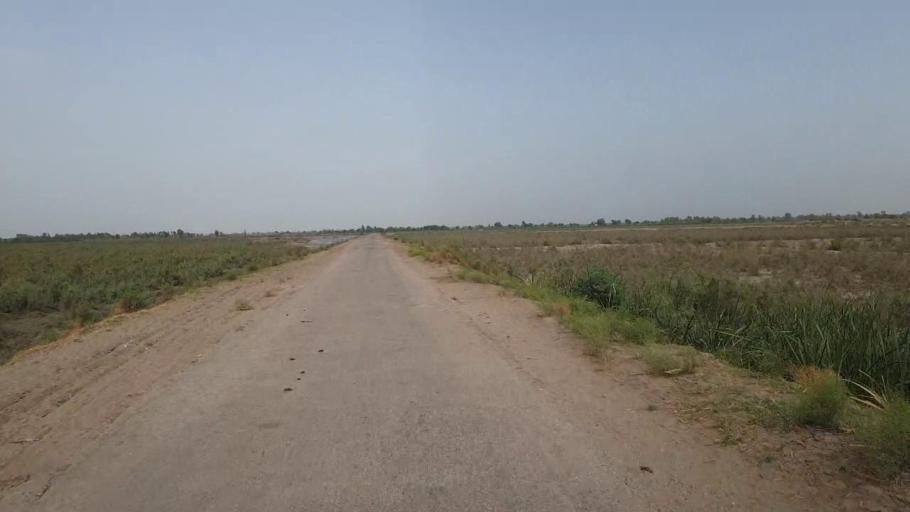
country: PK
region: Sindh
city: Daulatpur
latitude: 26.5462
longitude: 68.0809
